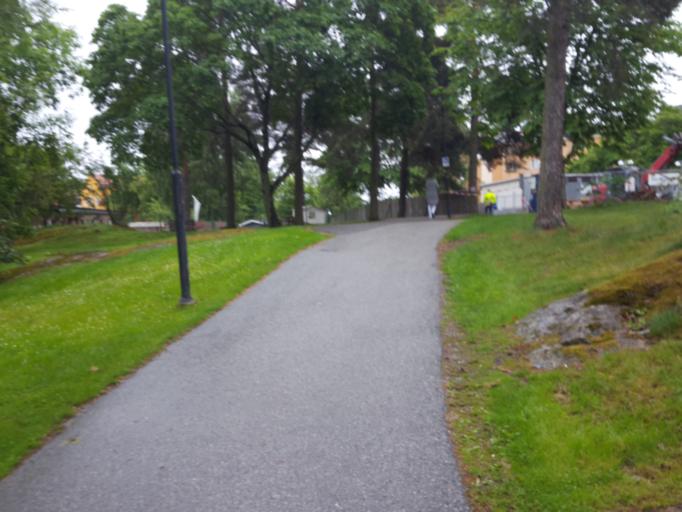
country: SE
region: Stockholm
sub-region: Norrtalje Kommun
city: Bergshamra
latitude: 59.3504
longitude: 18.0334
